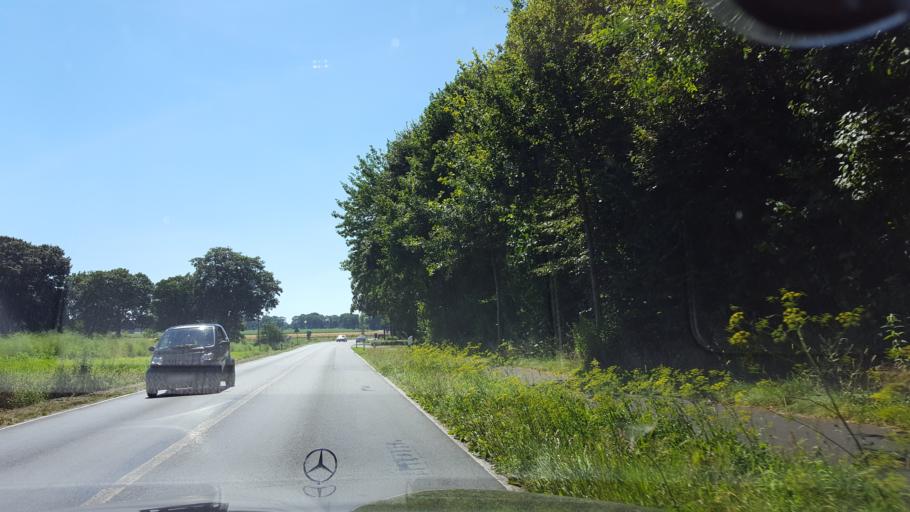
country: DE
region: North Rhine-Westphalia
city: Herten
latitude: 51.6402
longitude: 7.1554
